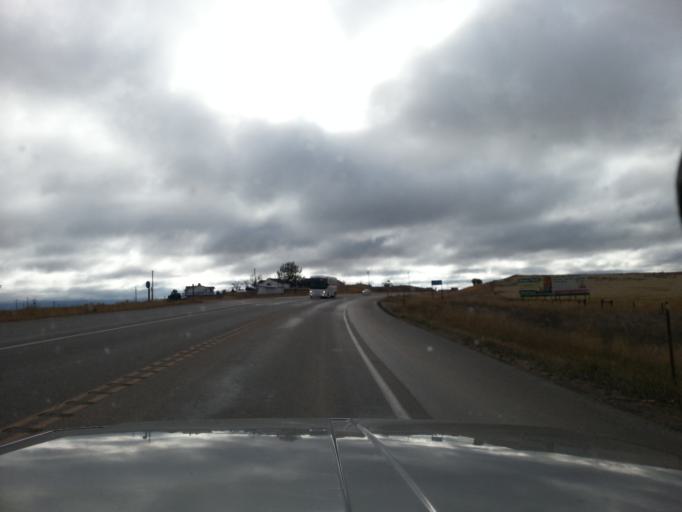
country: US
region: Wyoming
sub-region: Converse County
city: Douglas
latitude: 42.7823
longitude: -105.3738
